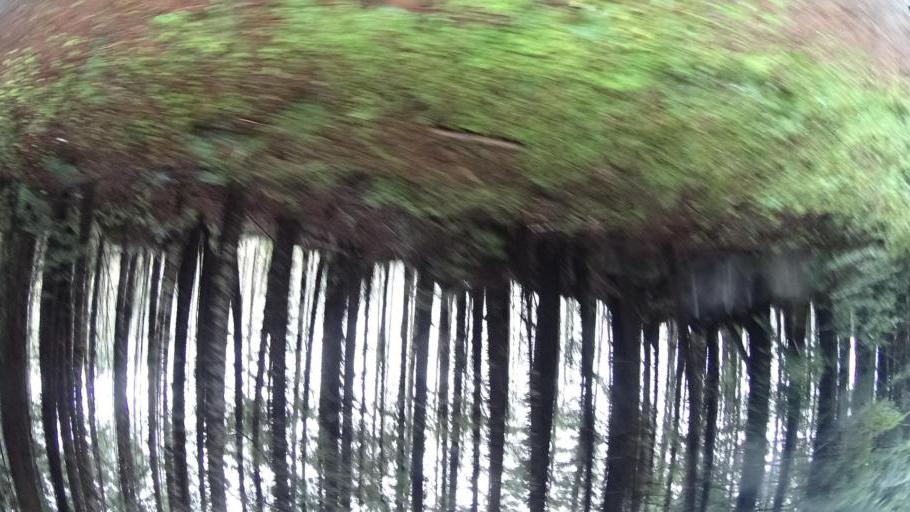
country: US
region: California
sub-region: Humboldt County
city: Westhaven-Moonstone
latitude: 41.2305
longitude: -123.9764
